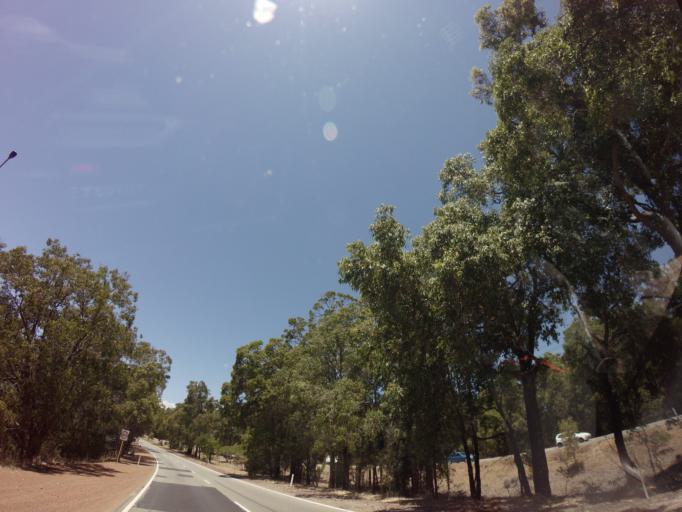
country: AU
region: Western Australia
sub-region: Mundaring
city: Darlington
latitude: -31.9027
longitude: 116.1051
